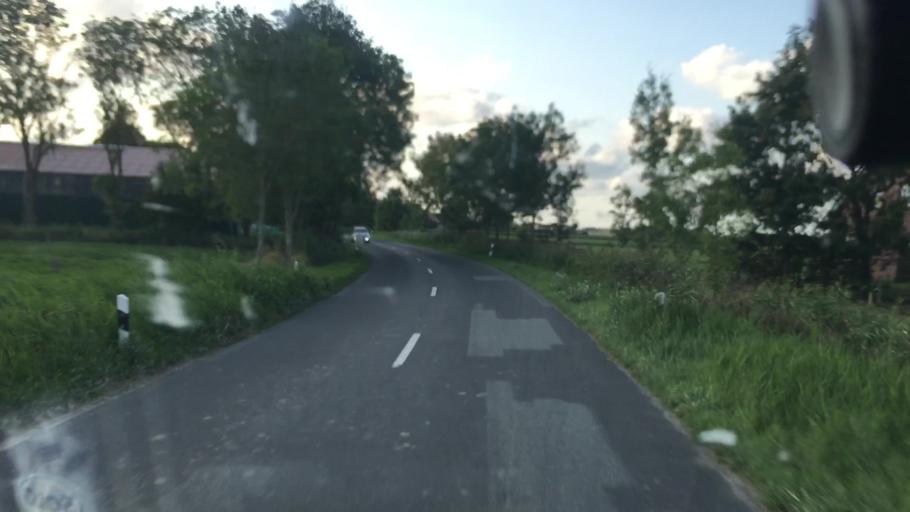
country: DE
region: Lower Saxony
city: Werdum
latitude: 53.6727
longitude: 7.7226
